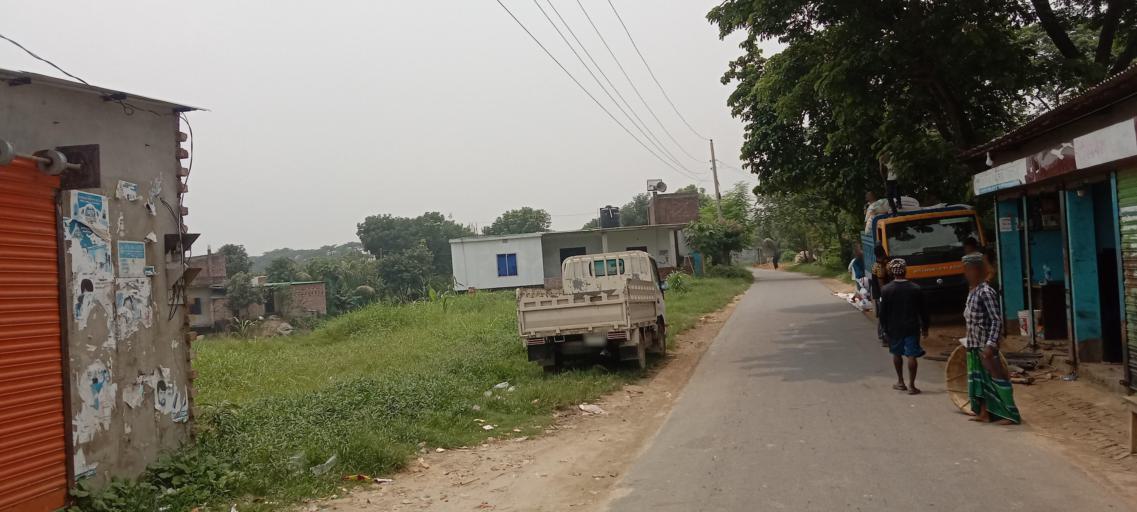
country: BD
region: Dhaka
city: Azimpur
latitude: 23.7460
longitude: 90.3028
